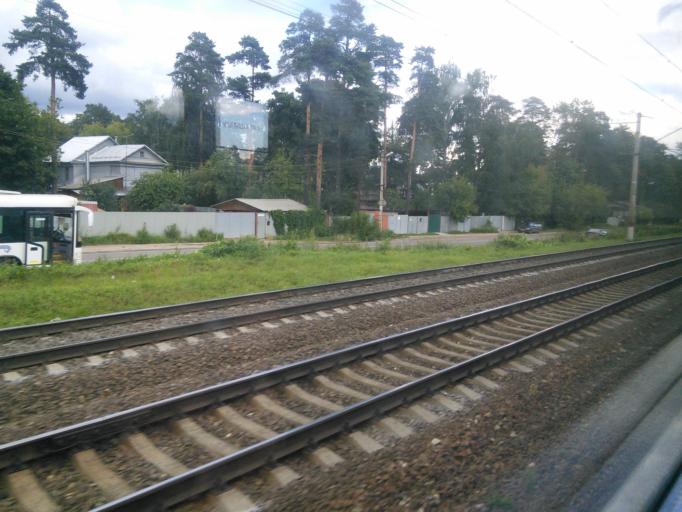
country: RU
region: Moskovskaya
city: Malakhovka
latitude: 55.6441
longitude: 38.0136
